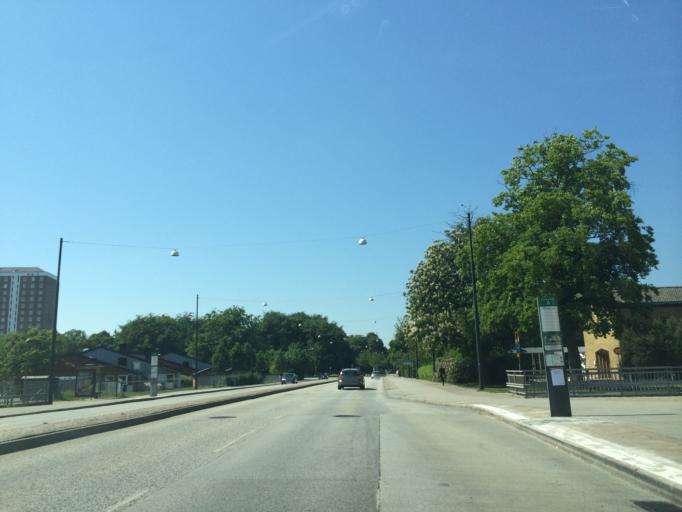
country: SE
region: Skane
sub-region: Malmo
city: Malmoe
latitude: 55.5858
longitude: 13.0026
